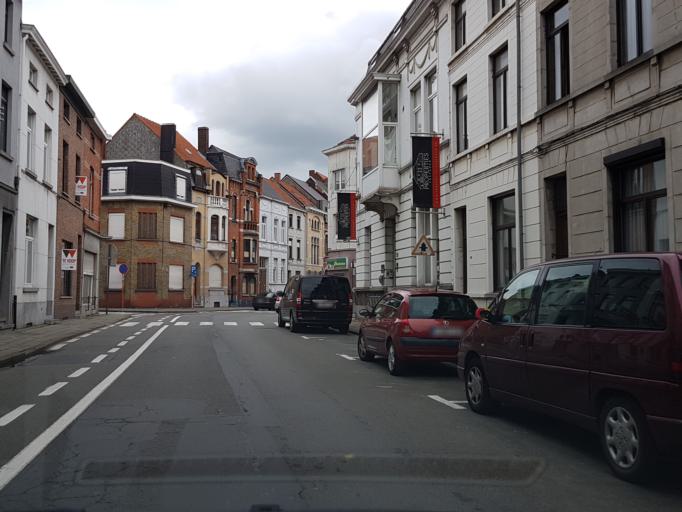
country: BE
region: Flanders
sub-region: Provincie Oost-Vlaanderen
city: Aalst
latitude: 50.9415
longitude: 4.0320
